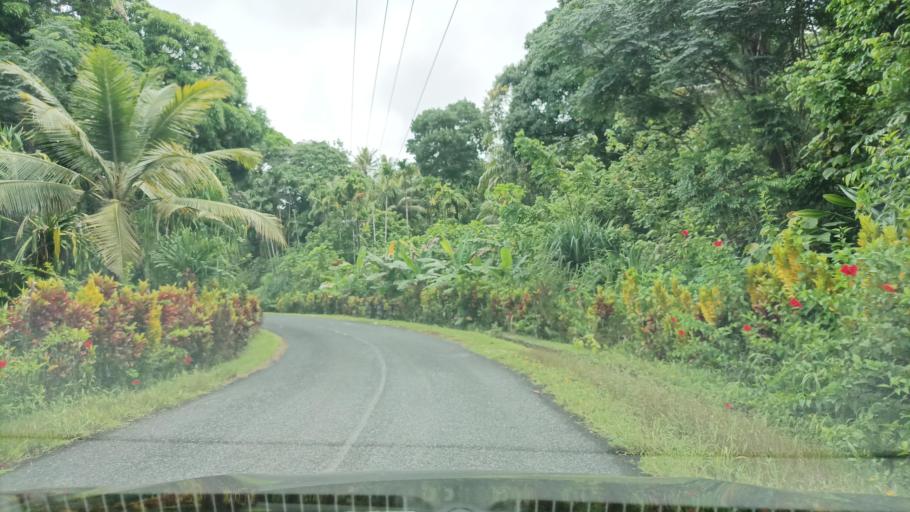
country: FM
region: Pohnpei
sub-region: Madolenihm Municipality
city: Madolenihm Municipality Government
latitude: 6.8241
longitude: 158.2980
